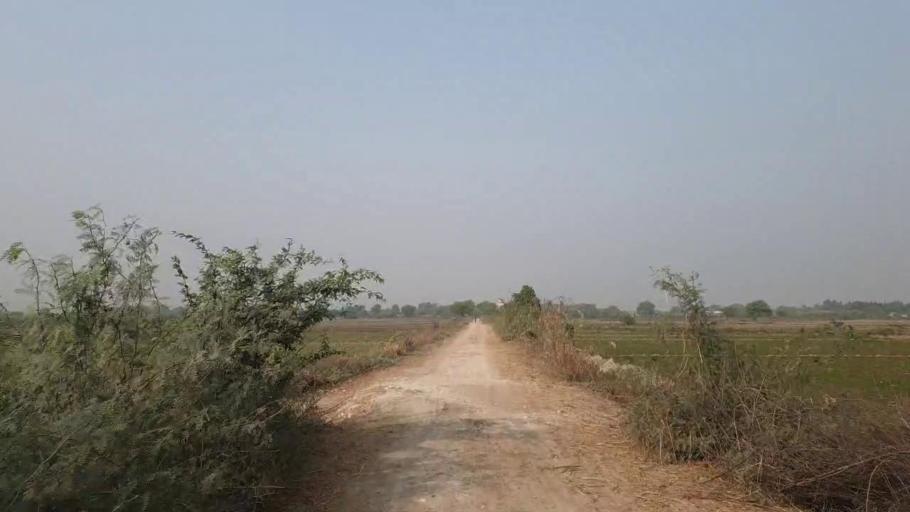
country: PK
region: Sindh
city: Tando Muhammad Khan
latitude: 25.1380
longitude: 68.6078
